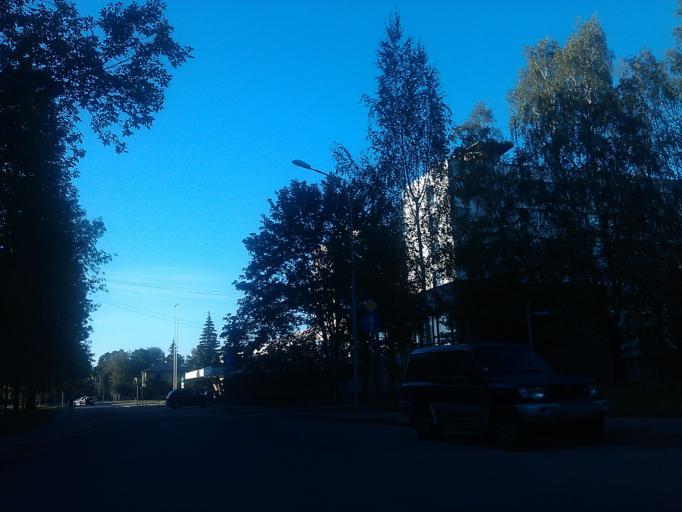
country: LV
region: Riga
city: Jaunciems
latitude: 56.9764
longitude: 24.1946
